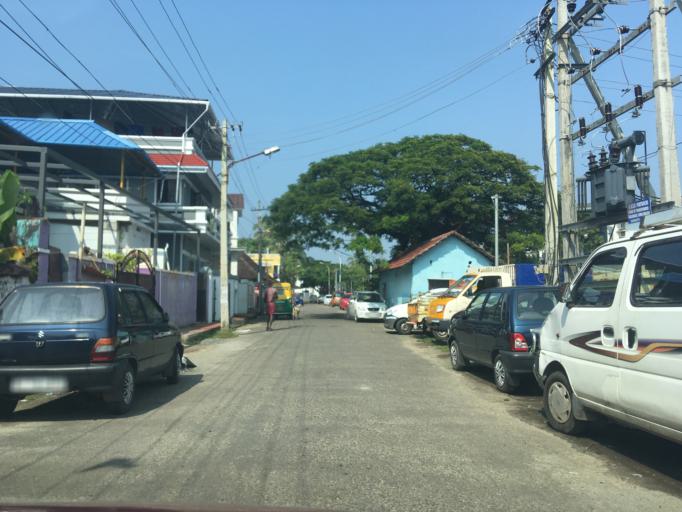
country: IN
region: Kerala
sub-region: Ernakulam
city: Cochin
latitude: 9.9649
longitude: 76.2493
